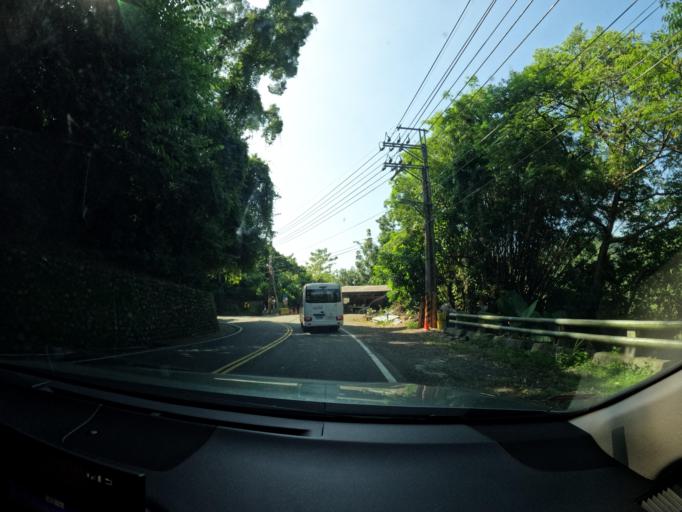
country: TW
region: Taiwan
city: Yujing
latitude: 23.0688
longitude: 120.6668
